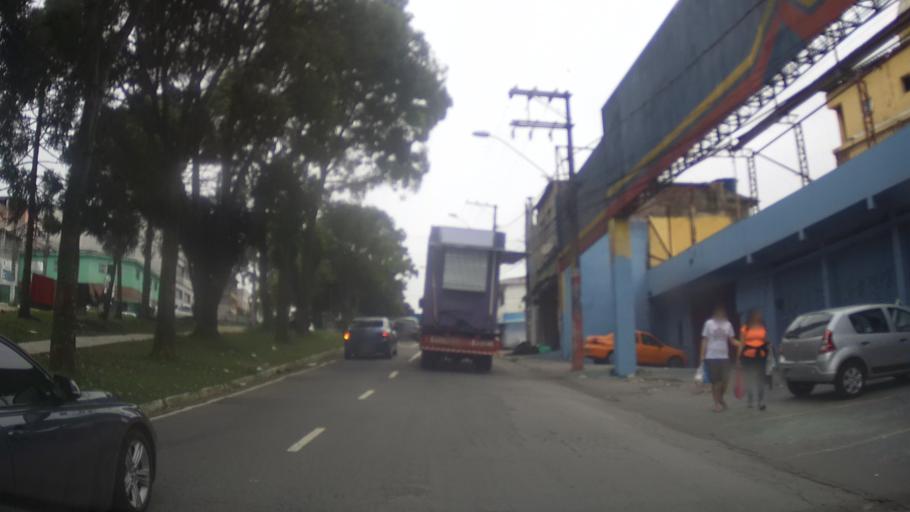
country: BR
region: Sao Paulo
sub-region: Guarulhos
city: Guarulhos
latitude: -23.4307
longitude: -46.5550
